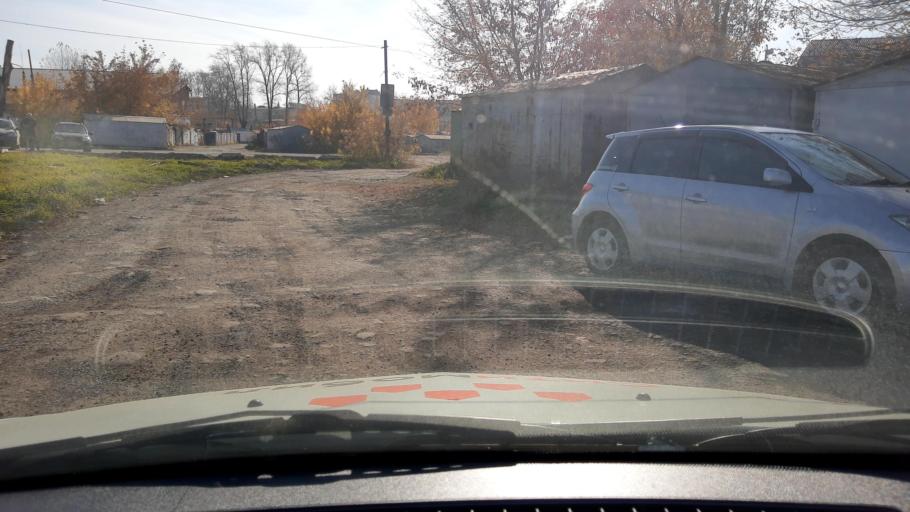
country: RU
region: Bashkortostan
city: Ufa
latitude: 54.8263
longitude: 56.1001
